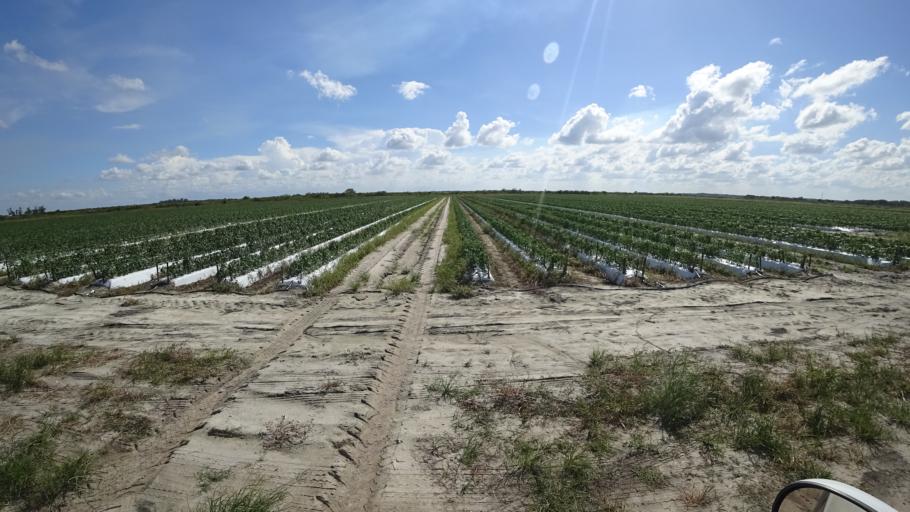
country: US
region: Florida
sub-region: DeSoto County
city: Arcadia
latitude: 27.3392
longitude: -82.0935
